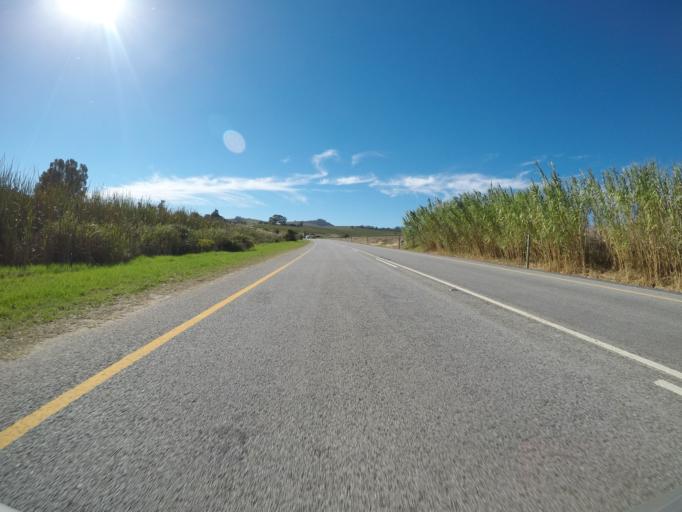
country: ZA
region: Western Cape
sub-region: Cape Winelands District Municipality
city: Stellenbosch
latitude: -33.9783
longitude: 18.7533
